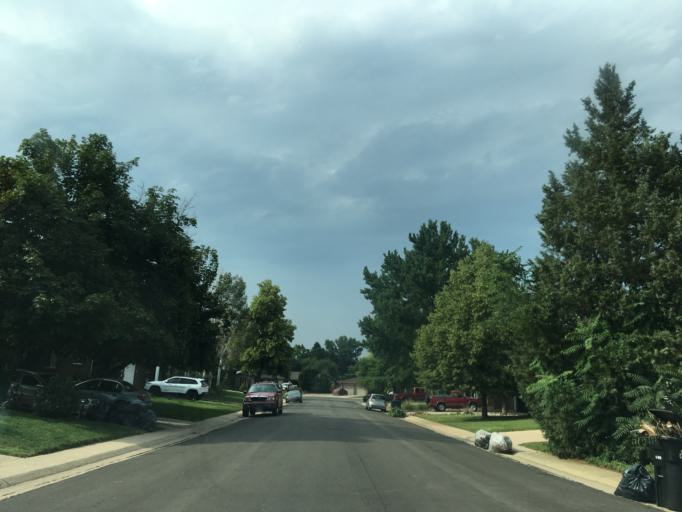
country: US
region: Colorado
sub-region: Jefferson County
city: Lakewood
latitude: 39.6766
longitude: -105.0612
